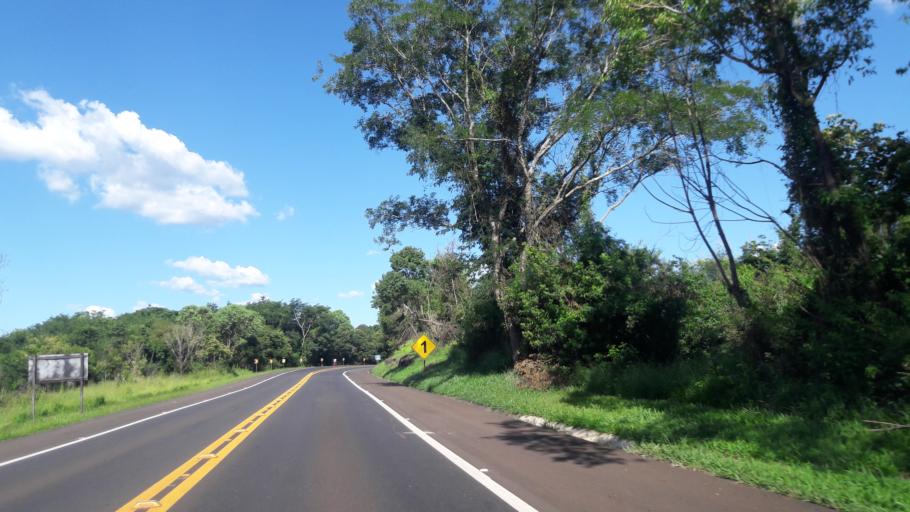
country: BR
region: Parana
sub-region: Laranjeiras Do Sul
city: Laranjeiras do Sul
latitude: -25.4197
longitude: -52.0358
